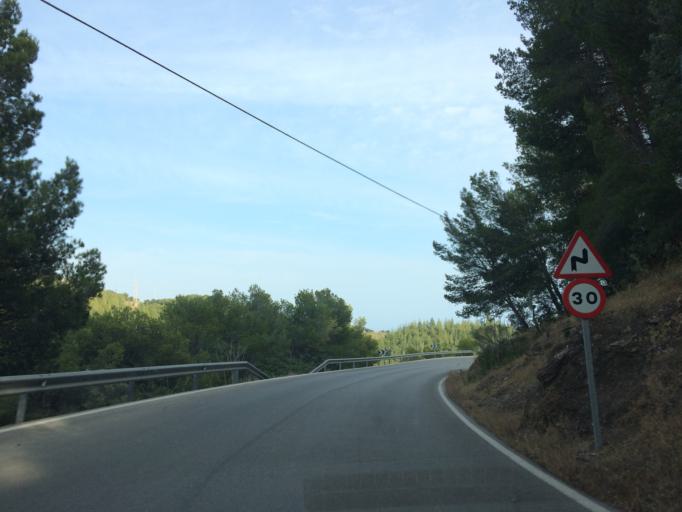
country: ES
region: Andalusia
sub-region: Provincia de Malaga
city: Malaga
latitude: 36.7614
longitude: -4.4068
